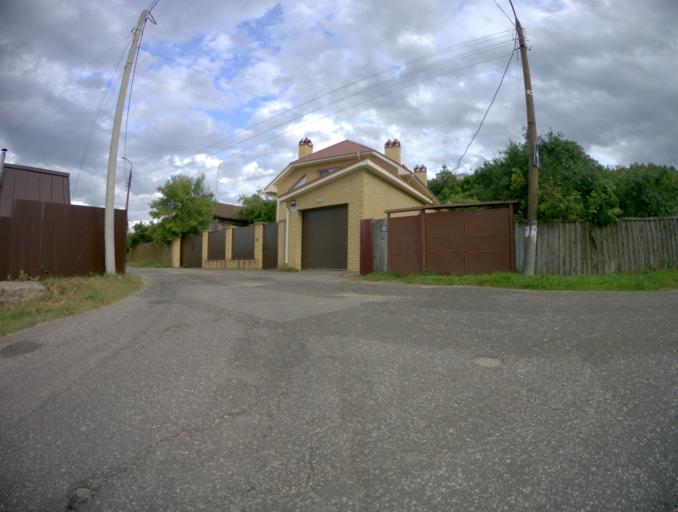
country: RU
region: Vladimir
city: Gorokhovets
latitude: 56.2064
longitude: 42.6723
